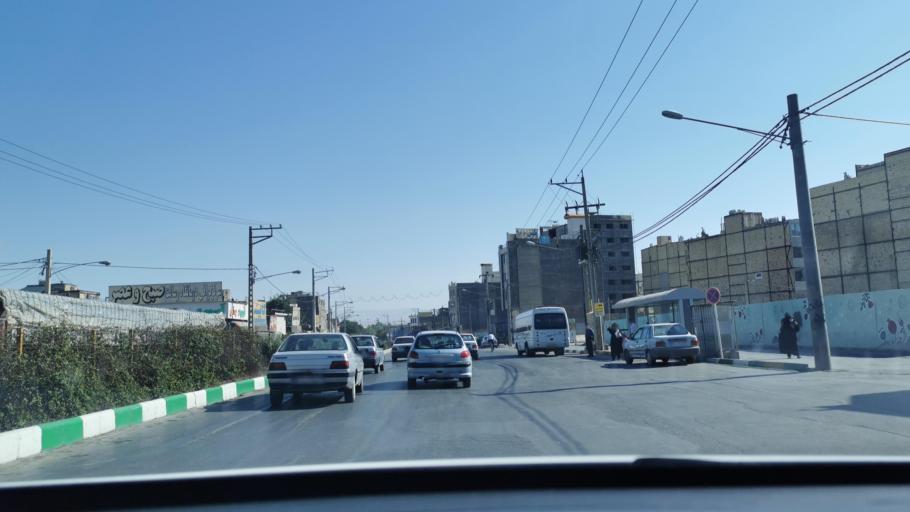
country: IR
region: Razavi Khorasan
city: Mashhad
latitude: 36.3221
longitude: 59.6408
